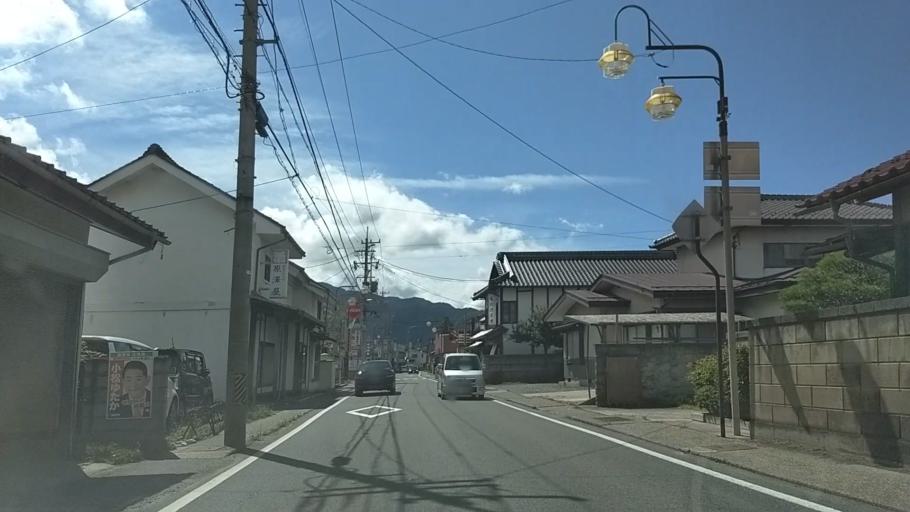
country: JP
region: Nagano
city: Suzaka
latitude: 36.6229
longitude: 138.2567
